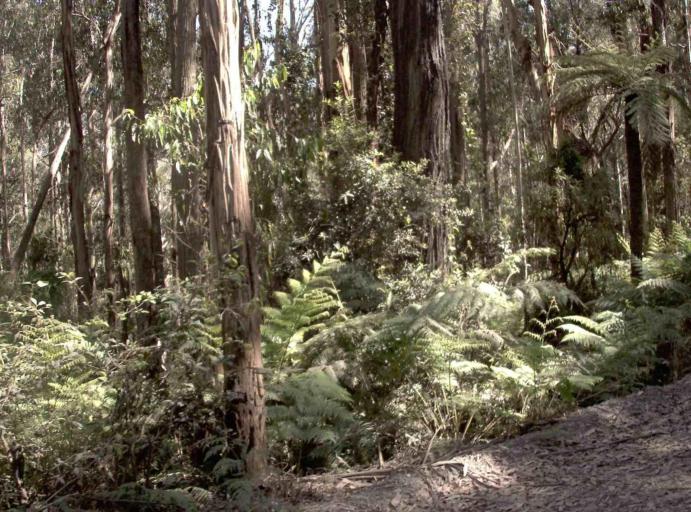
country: AU
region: New South Wales
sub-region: Bombala
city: Bombala
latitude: -37.2461
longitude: 148.7524
